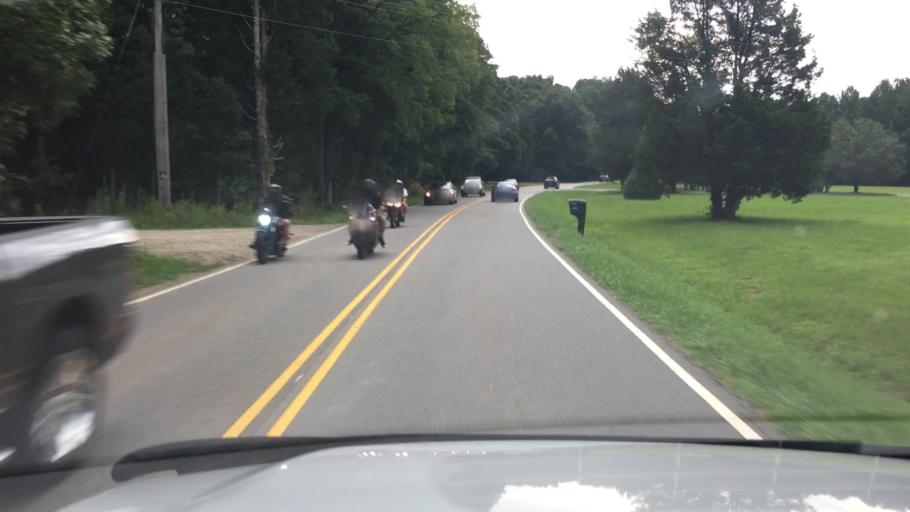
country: US
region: North Carolina
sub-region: Mecklenburg County
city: Huntersville
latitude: 35.3739
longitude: -80.9050
